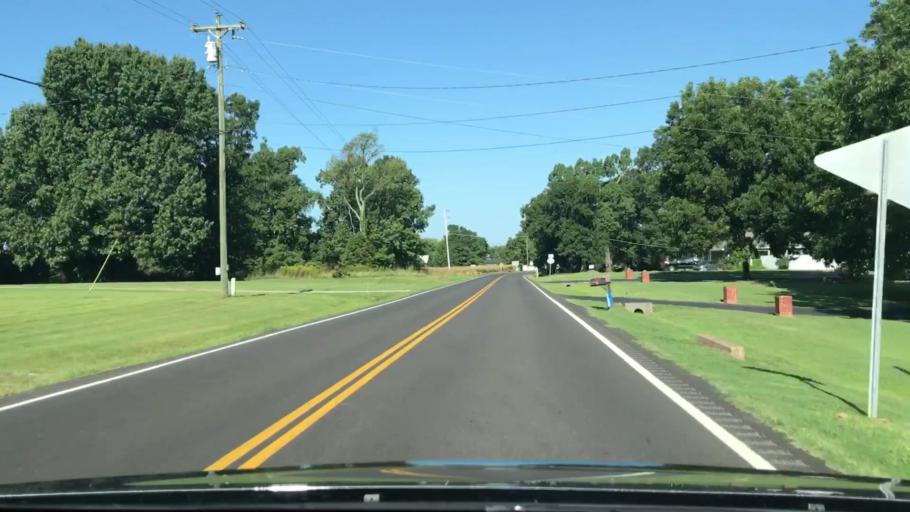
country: US
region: Kentucky
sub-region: Marshall County
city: Benton
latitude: 36.7682
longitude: -88.4354
